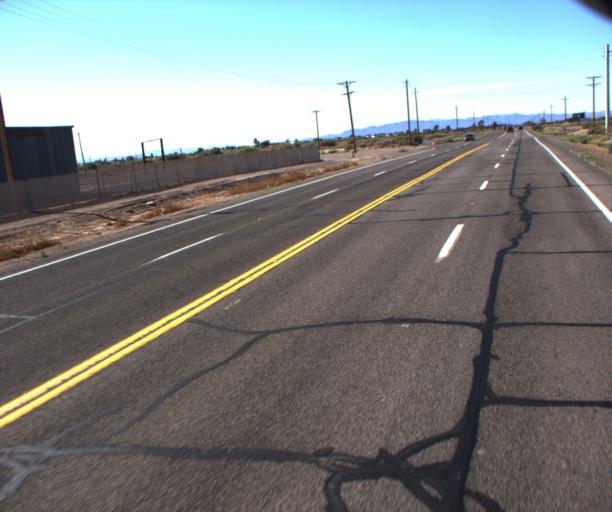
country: US
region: Arizona
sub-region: Mohave County
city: Mohave Valley
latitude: 34.9399
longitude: -114.5980
